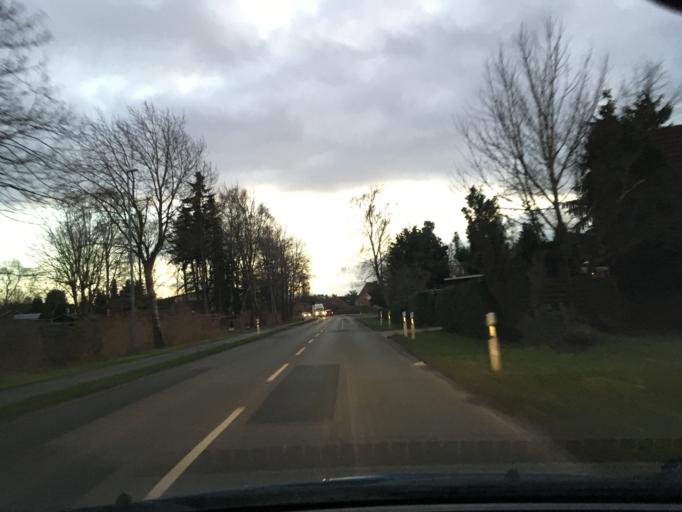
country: DE
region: Lower Saxony
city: Tespe
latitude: 53.3987
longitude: 10.4113
